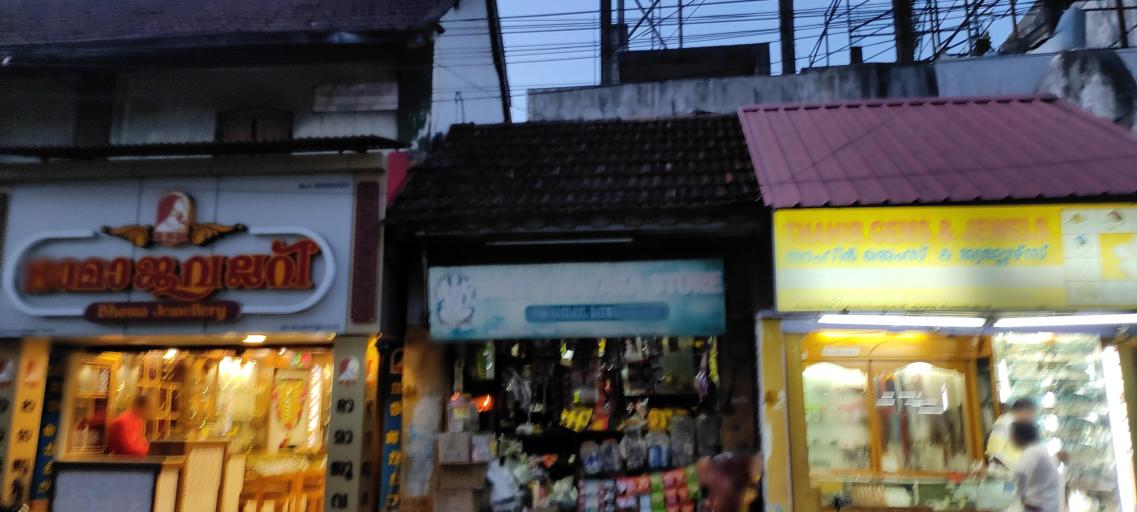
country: IN
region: Kerala
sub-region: Thiruvananthapuram
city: Thiruvananthapuram
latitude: 8.4817
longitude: 76.9569
